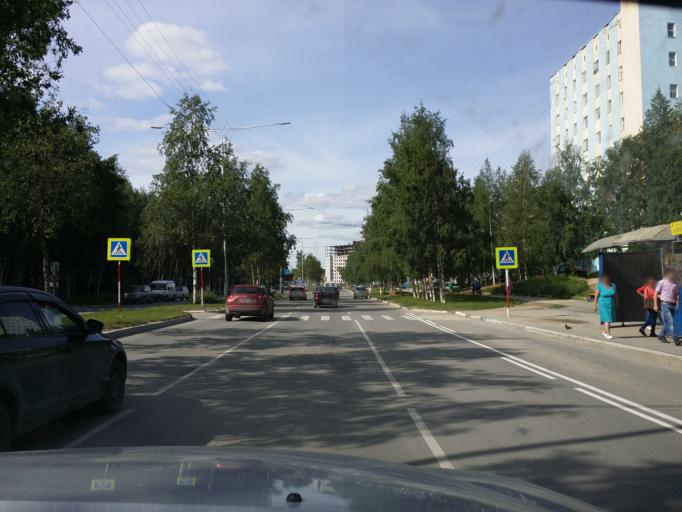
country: RU
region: Khanty-Mansiyskiy Avtonomnyy Okrug
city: Nizhnevartovsk
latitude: 60.9427
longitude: 76.5667
